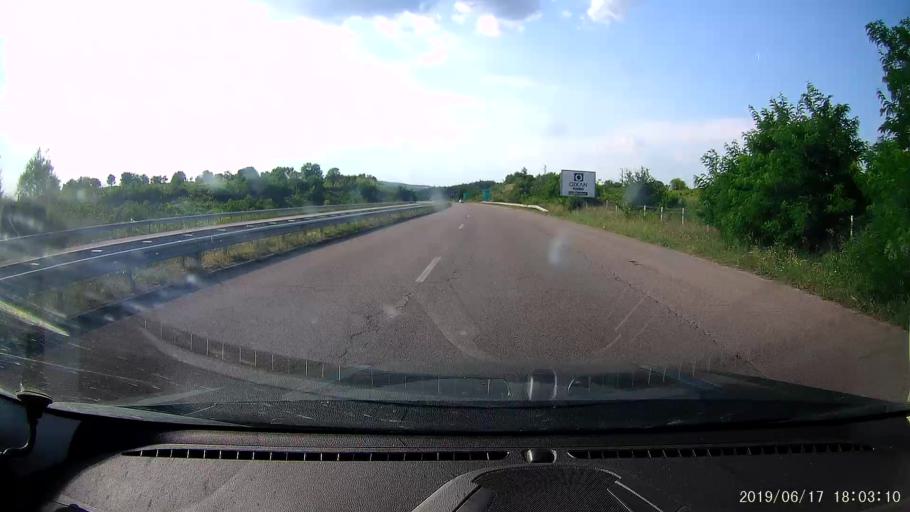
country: BG
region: Khaskovo
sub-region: Obshtina Svilengrad
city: Svilengrad
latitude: 41.7731
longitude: 26.2236
